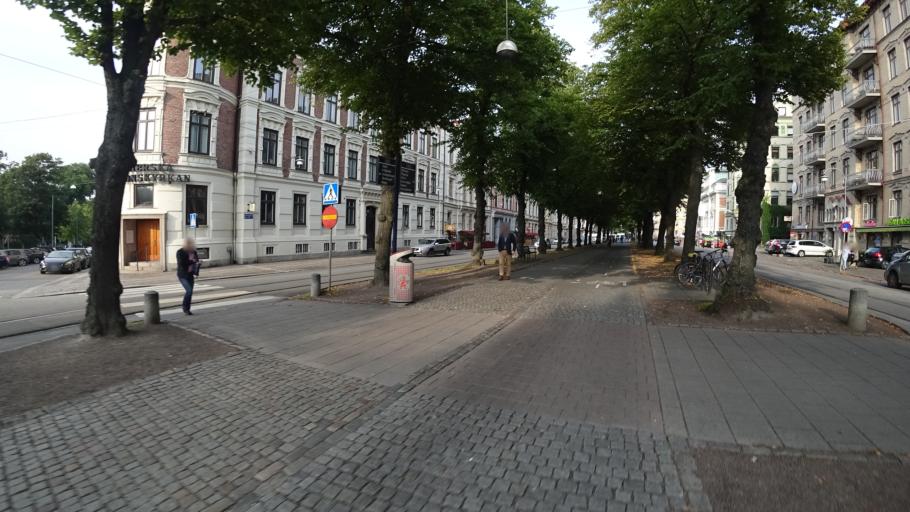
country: SE
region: Vaestra Goetaland
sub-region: Goteborg
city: Goeteborg
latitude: 57.6976
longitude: 11.9629
